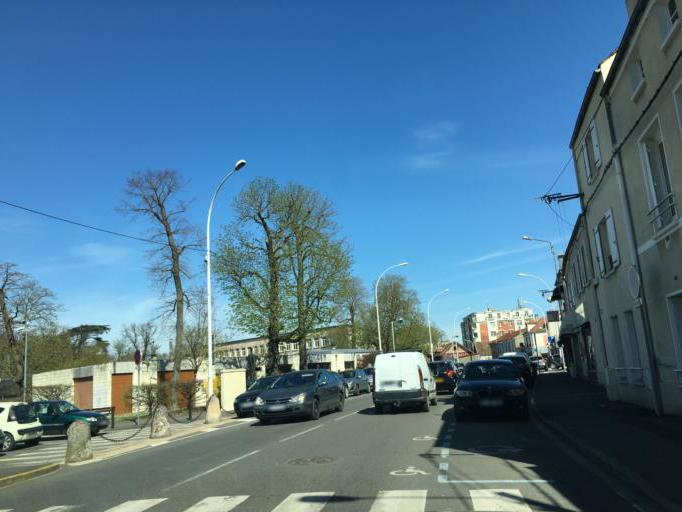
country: FR
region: Ile-de-France
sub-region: Departement de l'Essonne
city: Draveil
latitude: 48.6831
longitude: 2.4082
